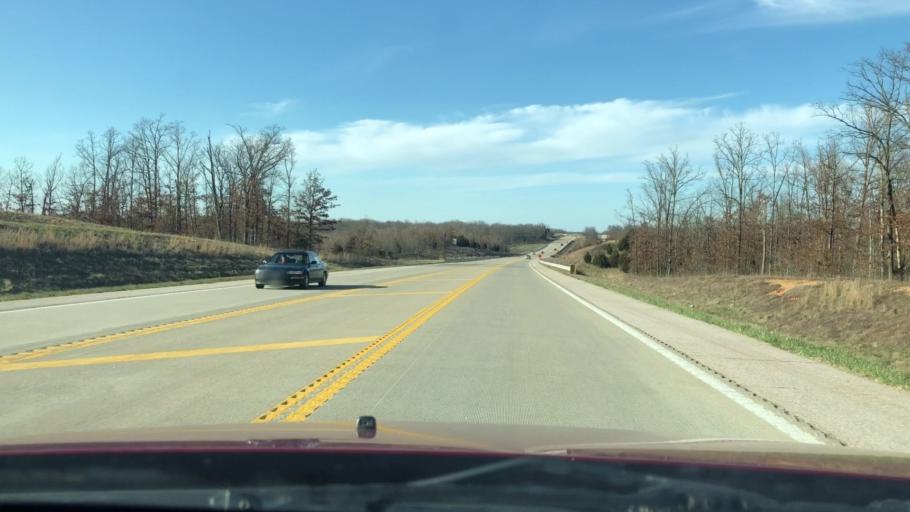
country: US
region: Missouri
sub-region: Camden County
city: Camdenton
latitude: 37.9388
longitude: -92.7155
